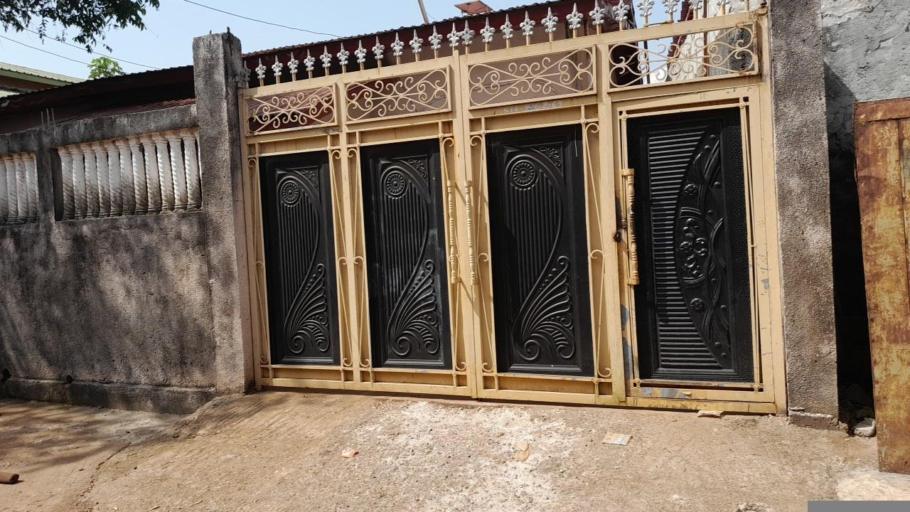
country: GN
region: Conakry
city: Conakry
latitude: 9.6111
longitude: -13.6150
